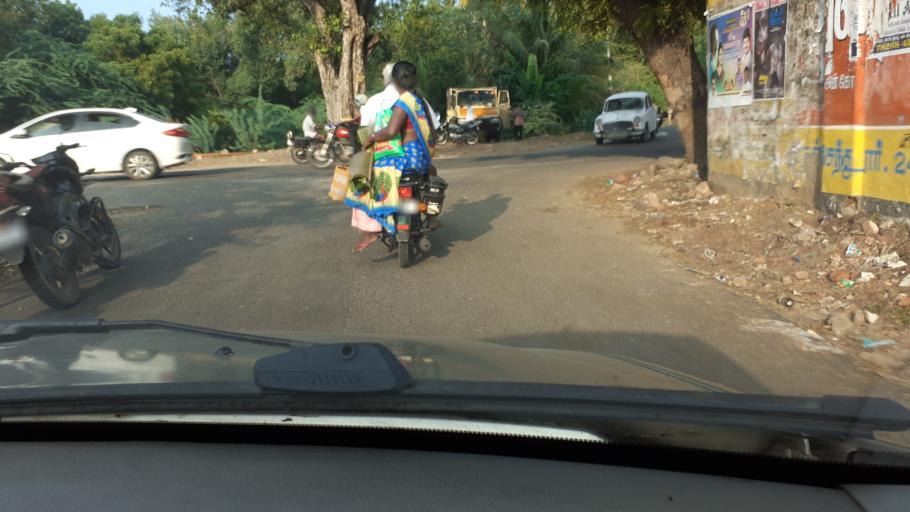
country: IN
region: Tamil Nadu
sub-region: Thoothukkudi
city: Alwar Tirunagari
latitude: 8.6031
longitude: 77.9781
